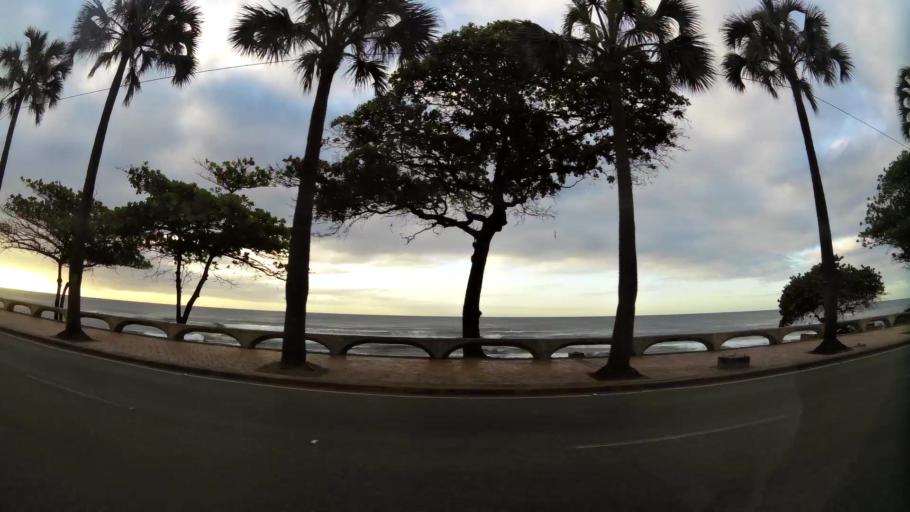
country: DO
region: Nacional
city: Ciudad Nueva
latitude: 18.4582
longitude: -69.9080
